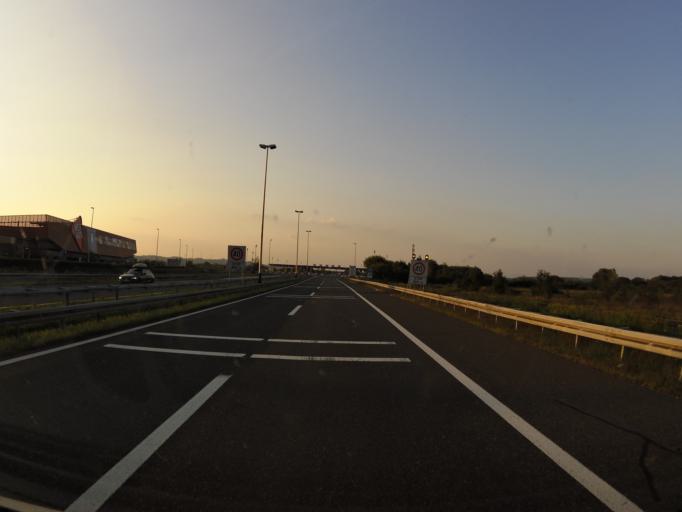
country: HR
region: Zagrebacka
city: Jablanovec
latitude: 45.8705
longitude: 15.8311
